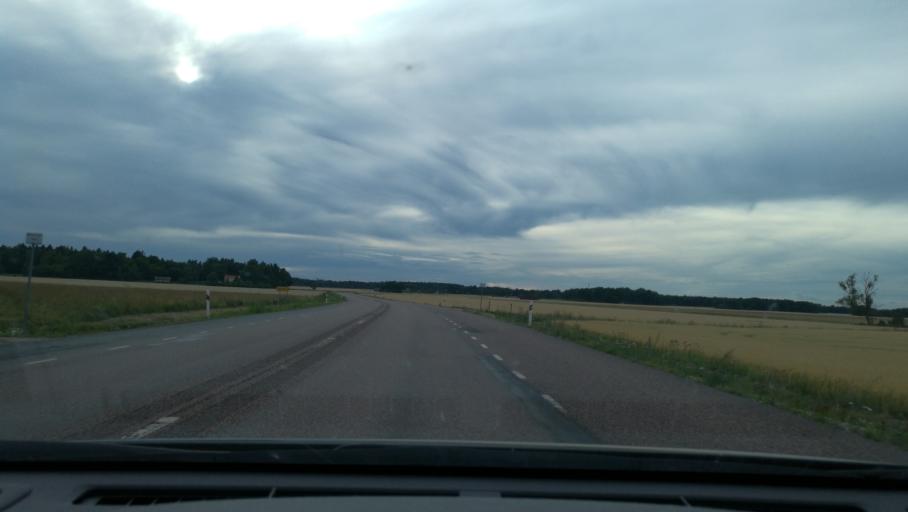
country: SE
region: Vaestmanland
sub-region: Kopings Kommun
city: Koping
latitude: 59.4567
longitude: 16.0192
